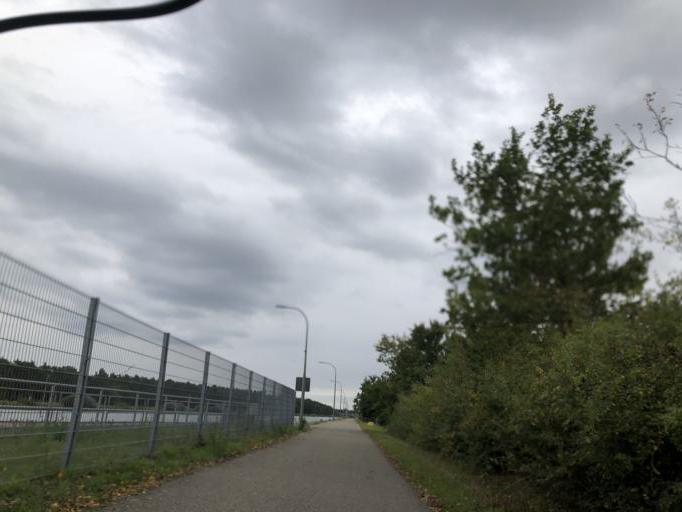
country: DE
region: Bavaria
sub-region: Regierungsbezirk Mittelfranken
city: Erlangen
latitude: 49.5541
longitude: 10.9693
